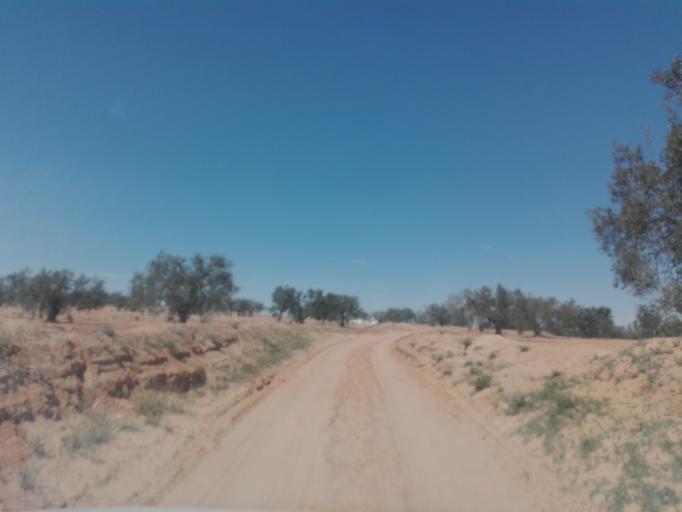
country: TN
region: Safaqis
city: Bi'r `Ali Bin Khalifah
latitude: 34.6631
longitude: 10.3117
